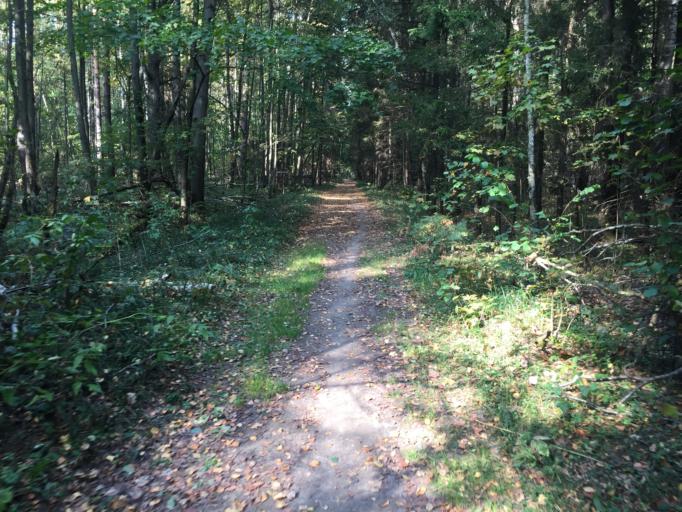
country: RU
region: Moscow
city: Babushkin
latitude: 55.8527
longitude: 37.7438
